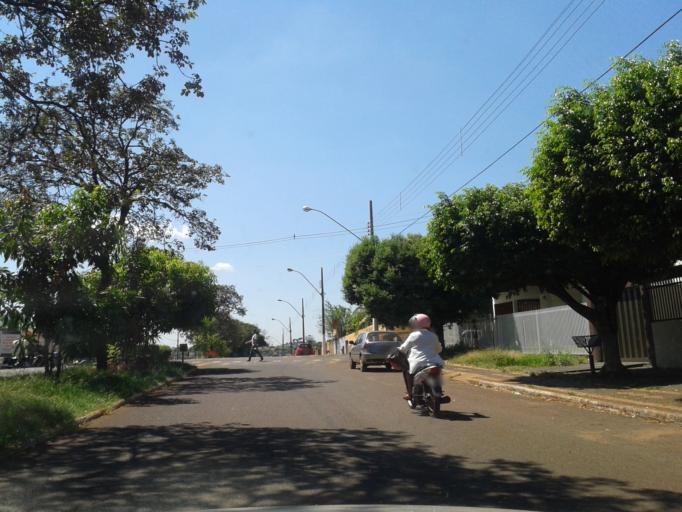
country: BR
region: Minas Gerais
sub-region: Ituiutaba
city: Ituiutaba
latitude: -18.9654
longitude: -49.4659
